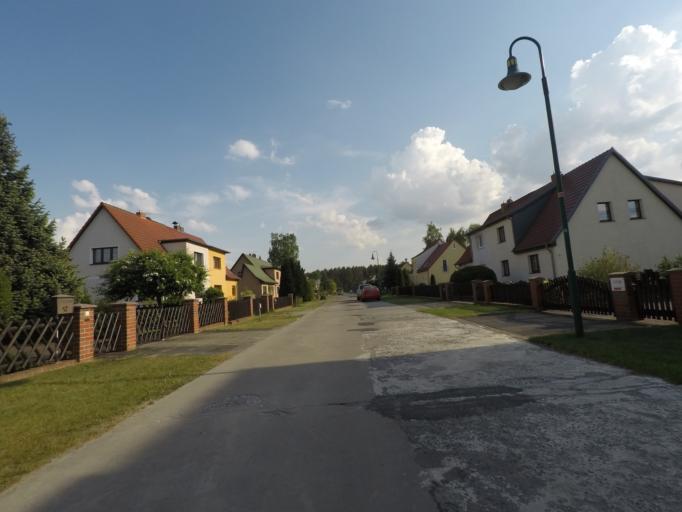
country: DE
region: Brandenburg
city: Melchow
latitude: 52.8344
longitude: 13.7212
